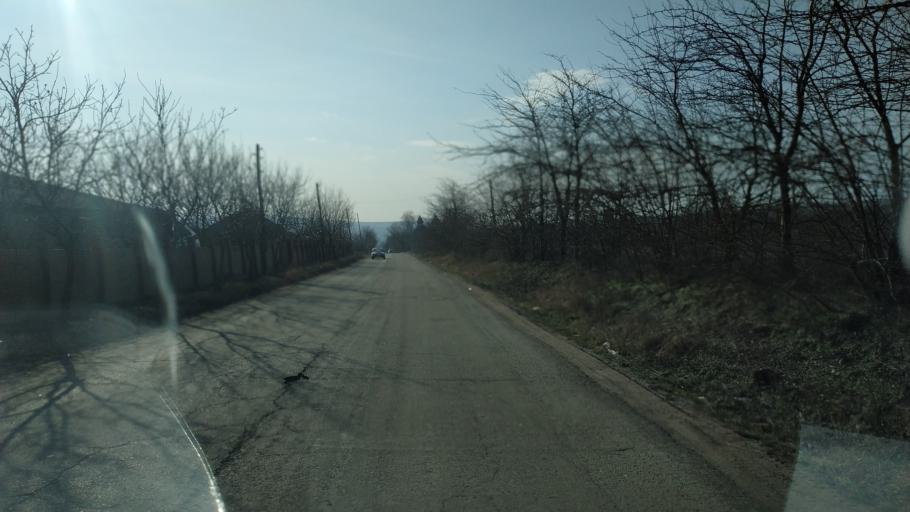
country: MD
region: Chisinau
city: Singera
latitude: 46.8430
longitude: 29.0256
